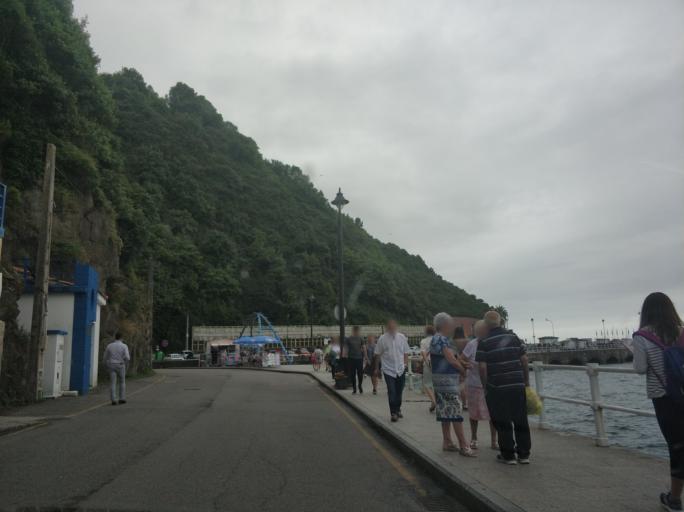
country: ES
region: Asturias
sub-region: Province of Asturias
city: Cudillero
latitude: 43.5636
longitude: -6.1465
